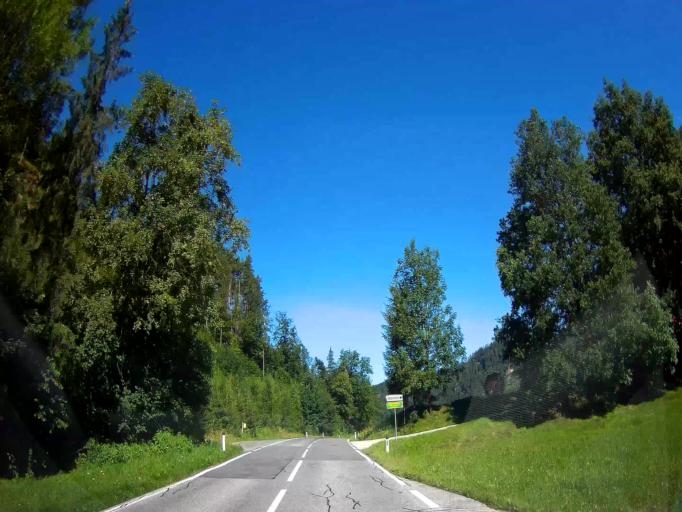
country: AT
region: Carinthia
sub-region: Politischer Bezirk Sankt Veit an der Glan
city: Bruckl
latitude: 46.7198
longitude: 14.5566
